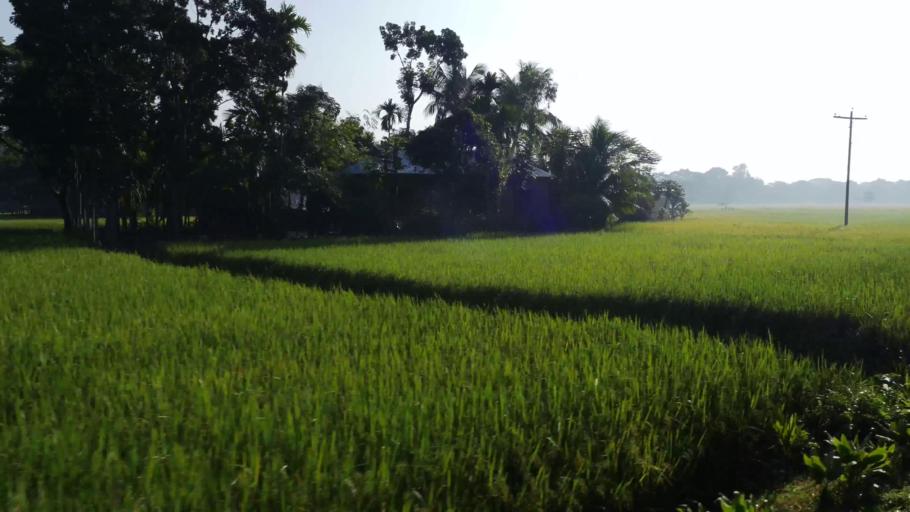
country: BD
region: Dhaka
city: Jamalpur
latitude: 24.8632
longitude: 90.0680
